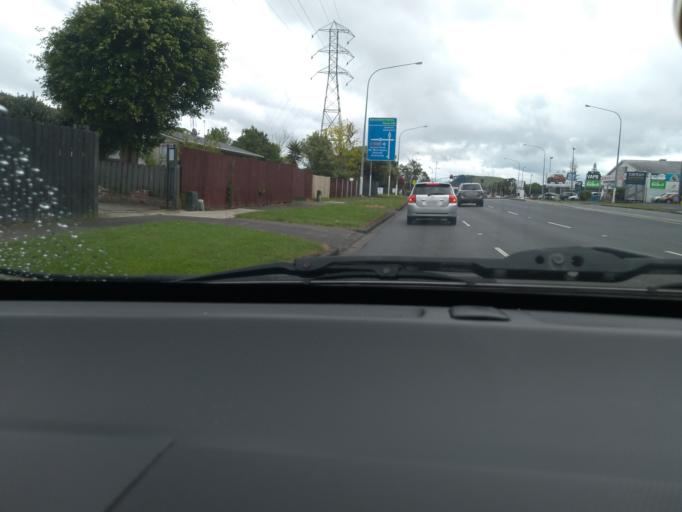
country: NZ
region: Auckland
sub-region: Auckland
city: Tamaki
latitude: -36.9163
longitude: 174.8724
